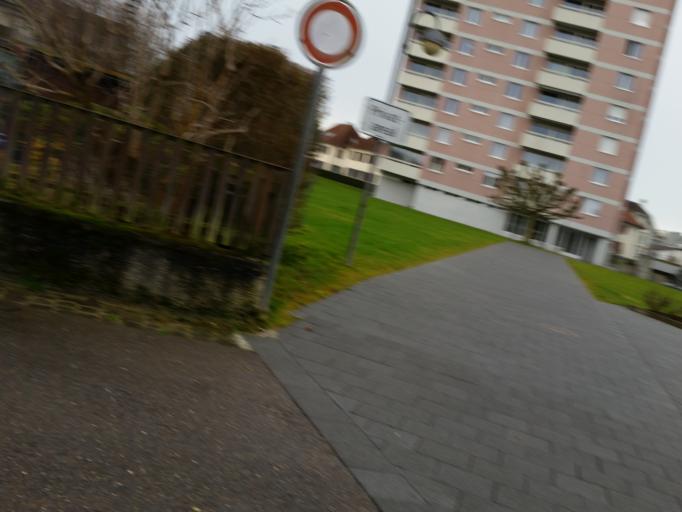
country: CH
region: Thurgau
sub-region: Arbon District
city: Salmsach
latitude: 47.5618
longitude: 9.3721
